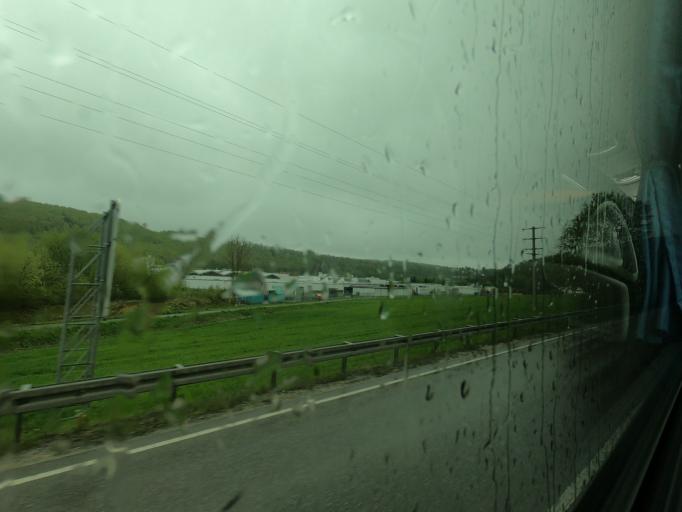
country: DE
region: Baden-Wuerttemberg
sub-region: Regierungsbezirk Stuttgart
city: Konigsbronn
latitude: 48.7370
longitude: 10.1313
